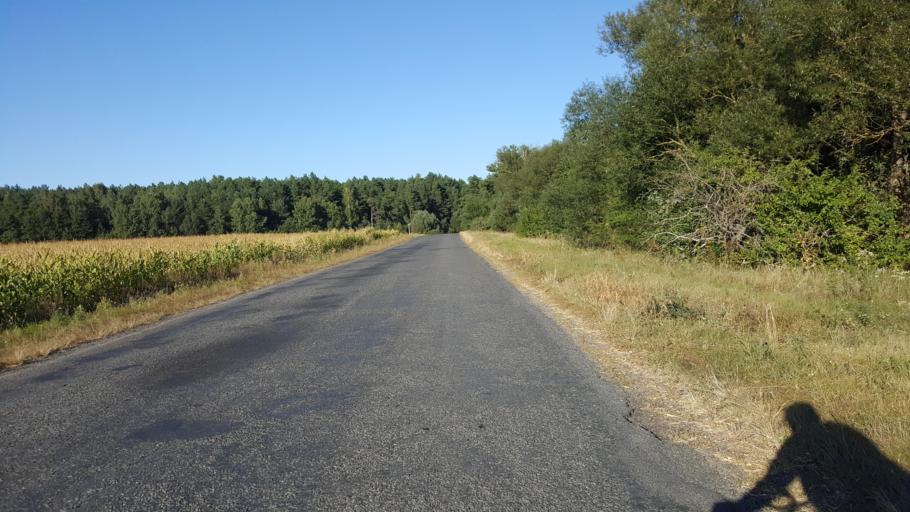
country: BY
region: Brest
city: Vysokaye
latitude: 52.3343
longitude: 23.2801
